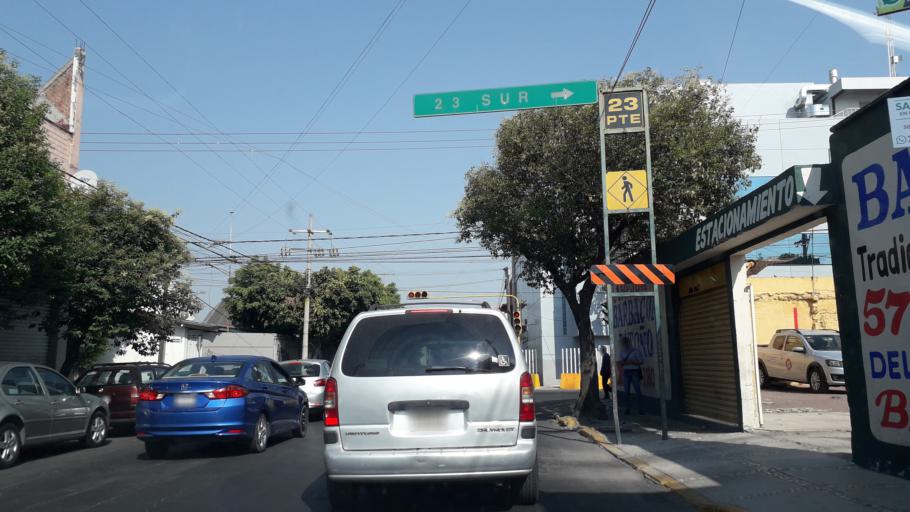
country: MX
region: Puebla
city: Puebla
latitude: 19.0442
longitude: -98.2196
